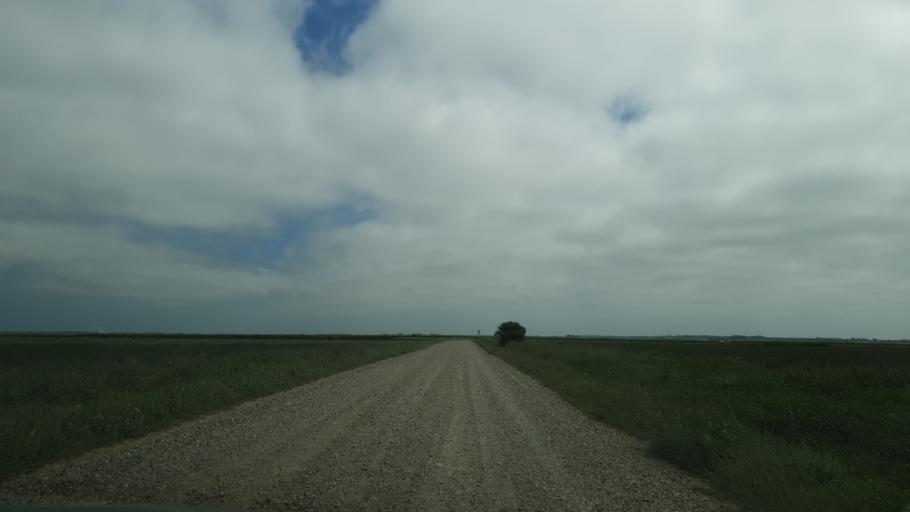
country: DK
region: Central Jutland
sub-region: Ringkobing-Skjern Kommune
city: Skjern
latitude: 55.9320
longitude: 8.4420
